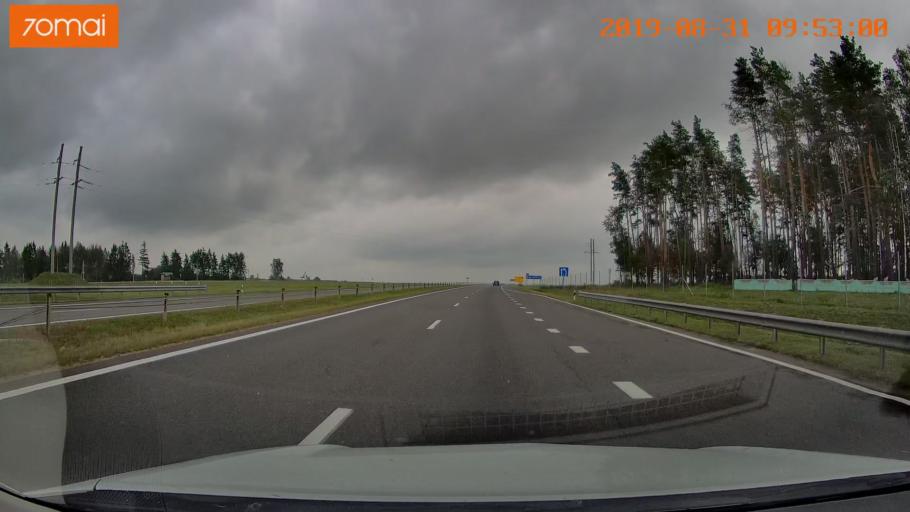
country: BY
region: Mogilev
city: Byalynichy
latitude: 53.9833
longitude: 29.7937
